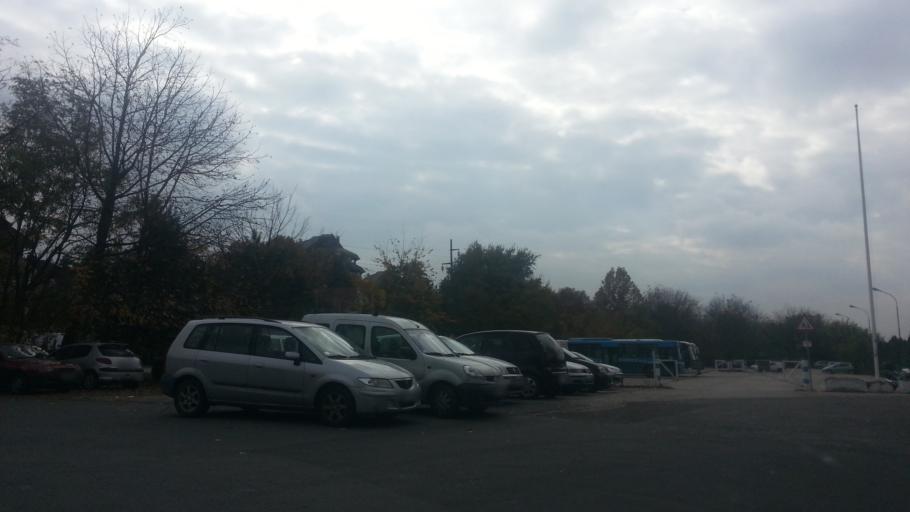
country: RS
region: Central Serbia
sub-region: Belgrade
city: Zemun
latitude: 44.8594
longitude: 20.3656
